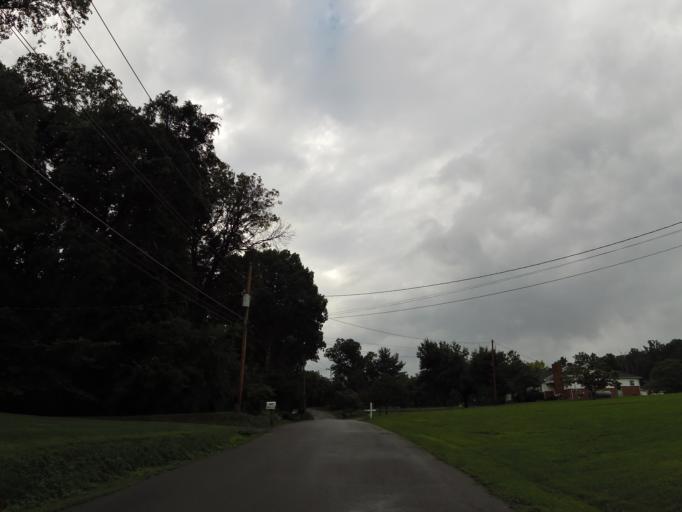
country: US
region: Tennessee
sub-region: Blount County
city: Eagleton Village
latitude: 35.7948
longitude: -83.9158
